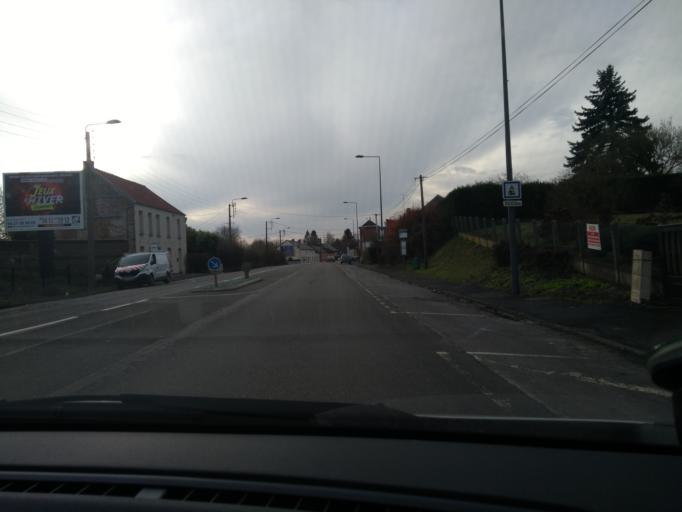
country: FR
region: Nord-Pas-de-Calais
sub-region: Departement du Nord
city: Maubeuge
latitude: 50.3033
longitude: 3.9776
